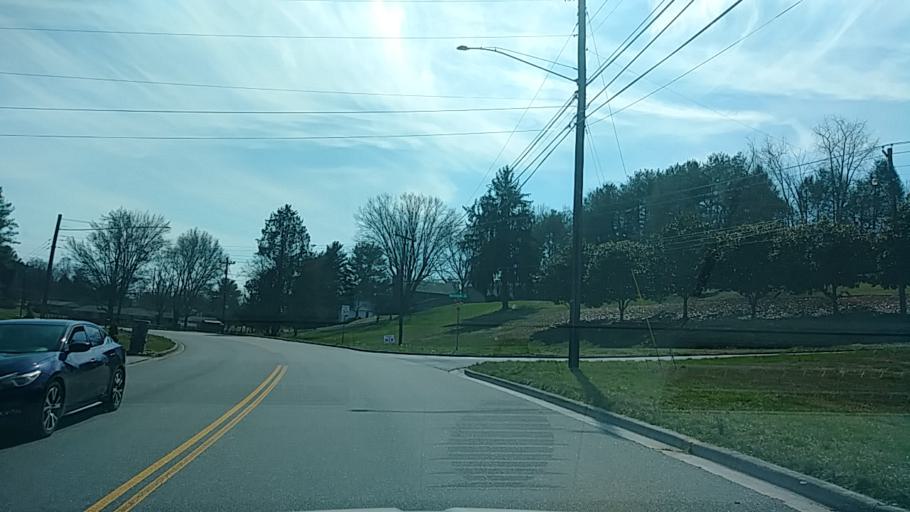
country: US
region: Tennessee
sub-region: Hamblen County
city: Morristown
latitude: 36.2189
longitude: -83.3218
